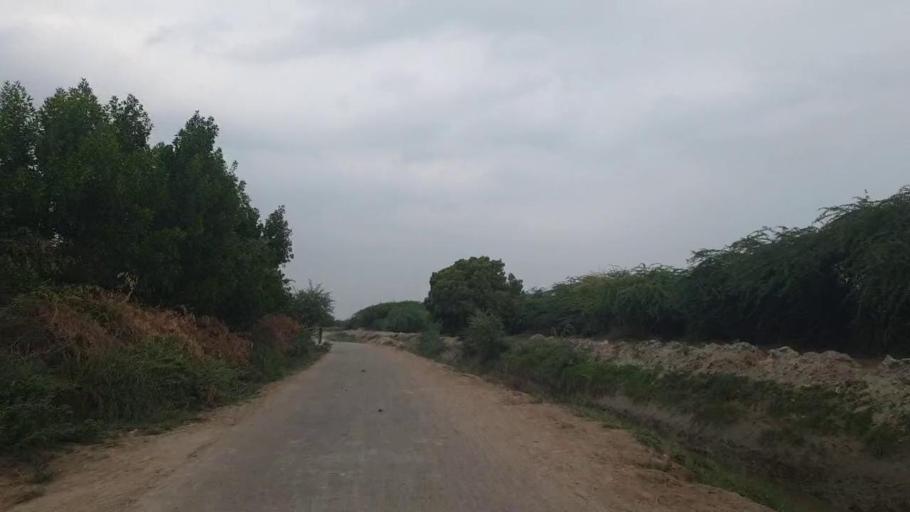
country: PK
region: Sindh
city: Badin
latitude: 24.6212
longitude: 68.6820
